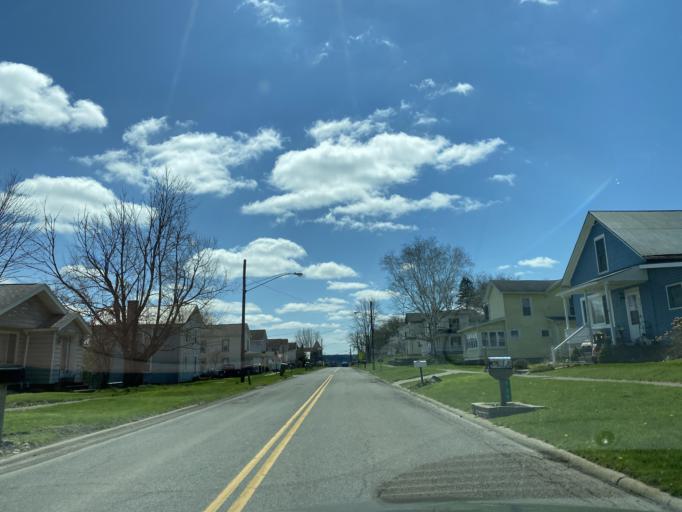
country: US
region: Ohio
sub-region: Wayne County
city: Shreve
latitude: 40.6882
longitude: -82.0223
